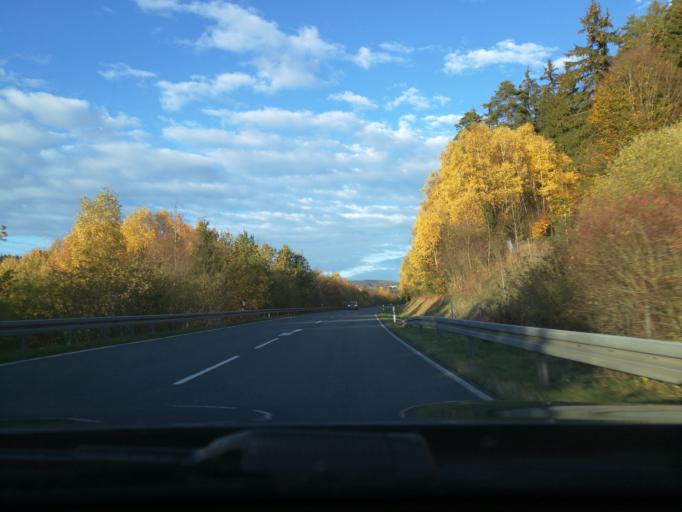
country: DE
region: Bavaria
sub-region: Regierungsbezirk Unterfranken
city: Wildflecken
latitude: 50.3672
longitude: 9.8973
